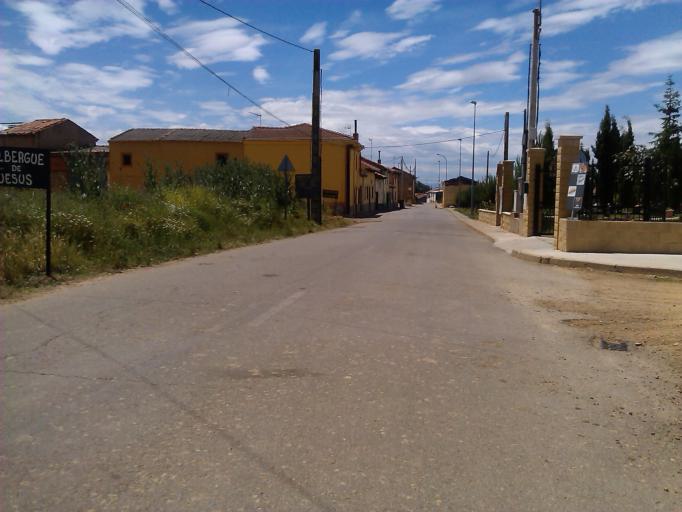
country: ES
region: Castille and Leon
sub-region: Provincia de Leon
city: Chozas de Abajo
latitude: 42.4848
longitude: -5.7253
